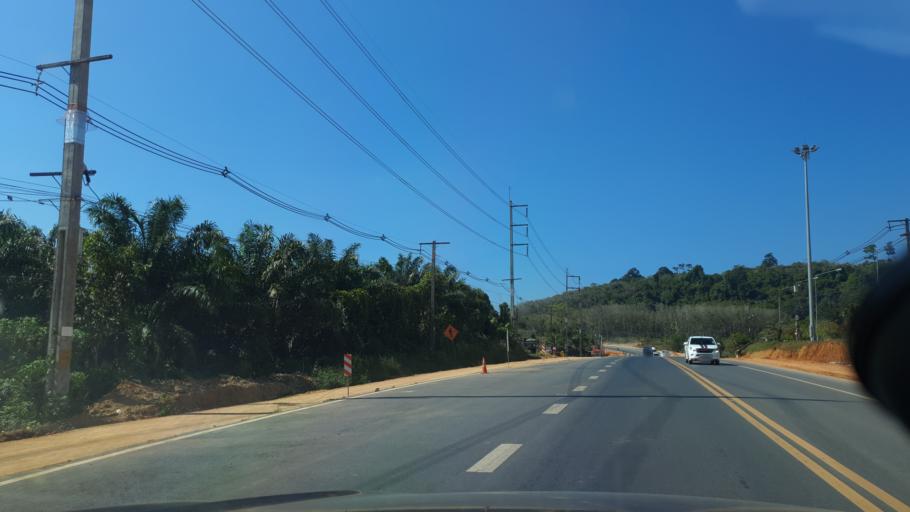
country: TH
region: Phangnga
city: Ban Khao Lak
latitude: 8.6053
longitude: 98.2507
